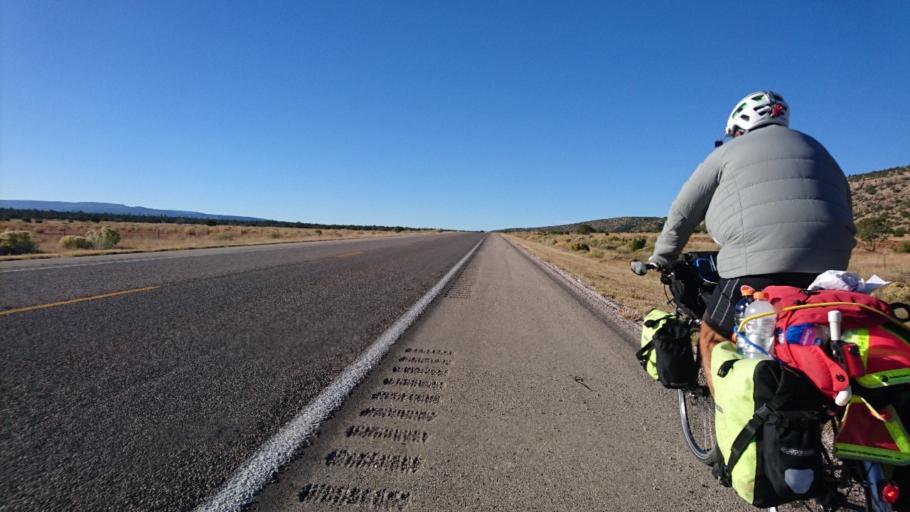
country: US
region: New Mexico
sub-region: Cibola County
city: Grants
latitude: 34.9892
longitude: -107.9016
